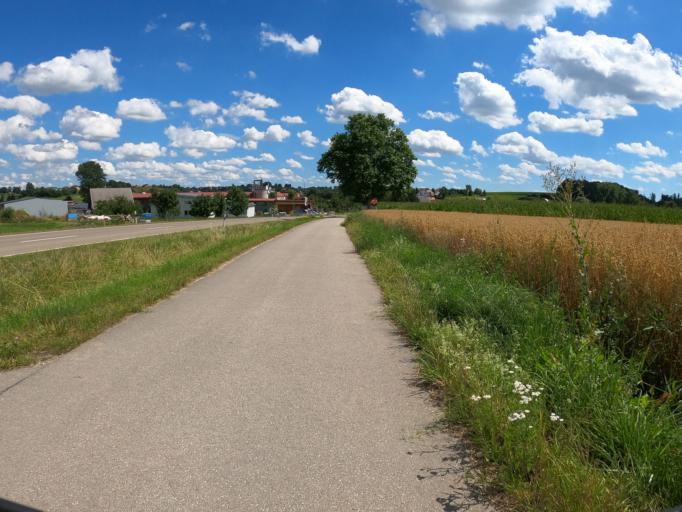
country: DE
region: Bavaria
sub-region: Swabia
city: Pfaffenhofen an der Roth
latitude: 48.4013
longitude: 10.1797
